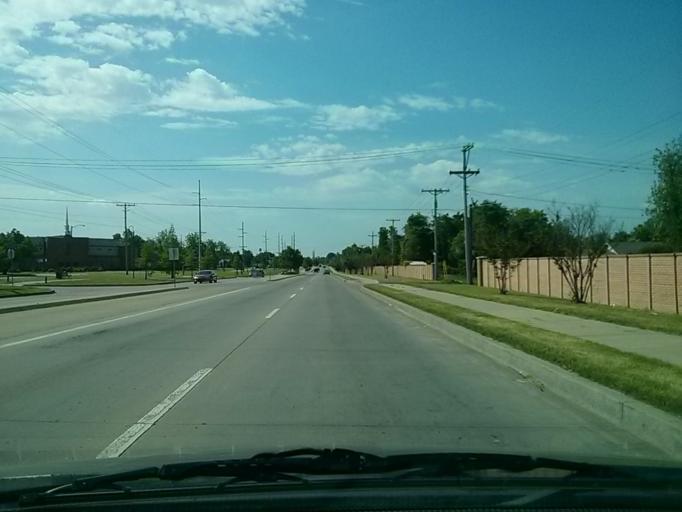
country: US
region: Oklahoma
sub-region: Tulsa County
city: Tulsa
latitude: 36.1883
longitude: -95.9760
